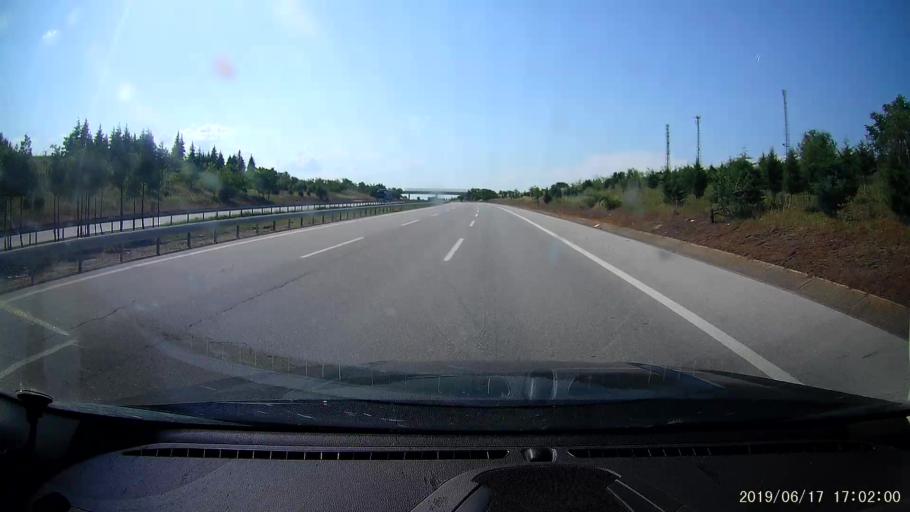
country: TR
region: Edirne
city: Haskoy
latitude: 41.6348
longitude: 26.7916
